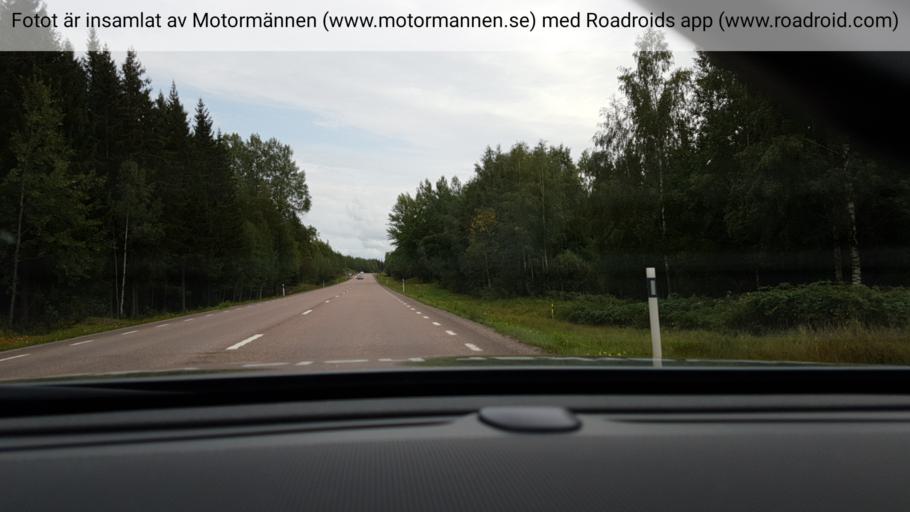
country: SE
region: Dalarna
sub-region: Faluns Kommun
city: Falun
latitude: 60.6496
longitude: 15.5611
